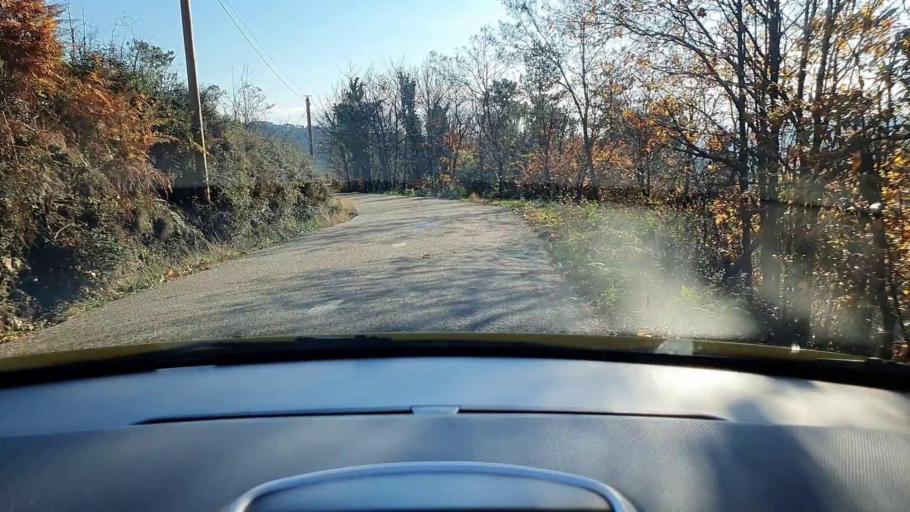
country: FR
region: Languedoc-Roussillon
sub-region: Departement du Gard
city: Branoux-les-Taillades
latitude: 44.2815
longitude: 3.9568
